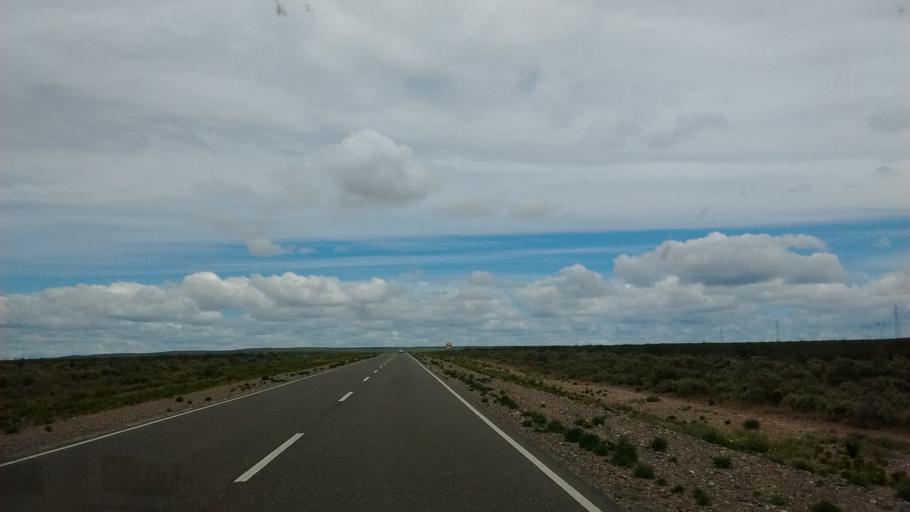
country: AR
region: Neuquen
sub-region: Departamento de Picun Leufu
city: Picun Leufu
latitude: -39.7051
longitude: -69.5024
